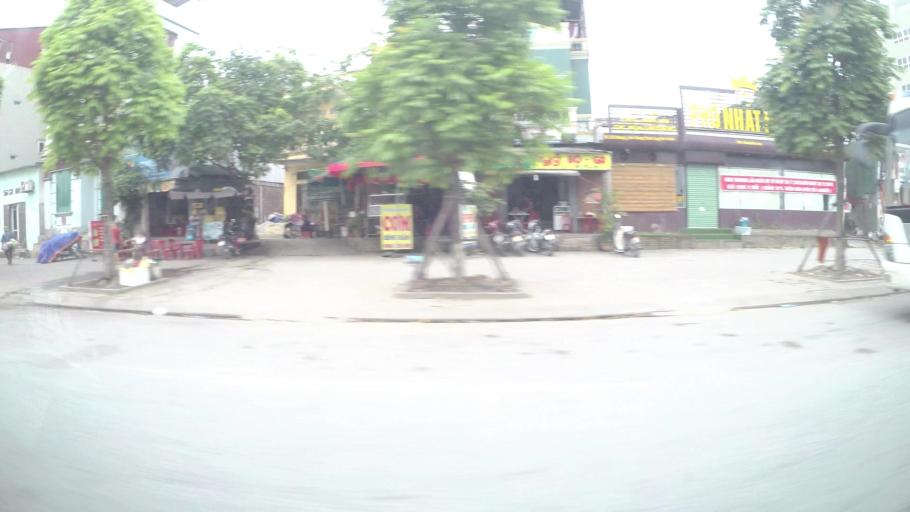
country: VN
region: Ha Noi
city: Hoan Kiem
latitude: 21.0609
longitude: 105.8829
